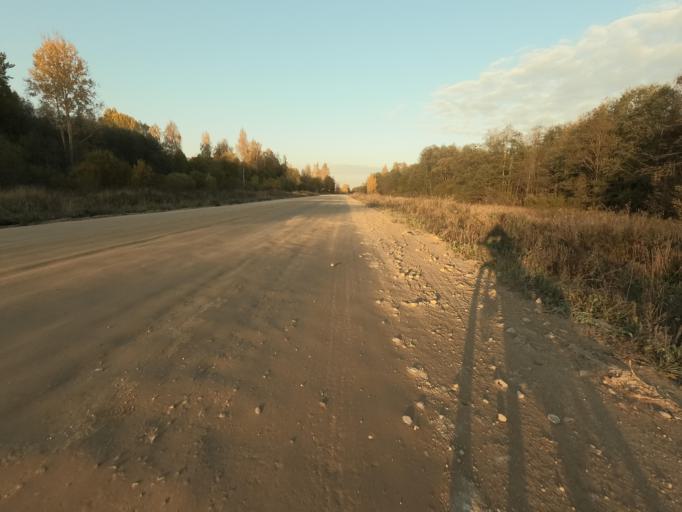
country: RU
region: Leningrad
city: Lyuban'
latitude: 59.0176
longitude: 31.0873
